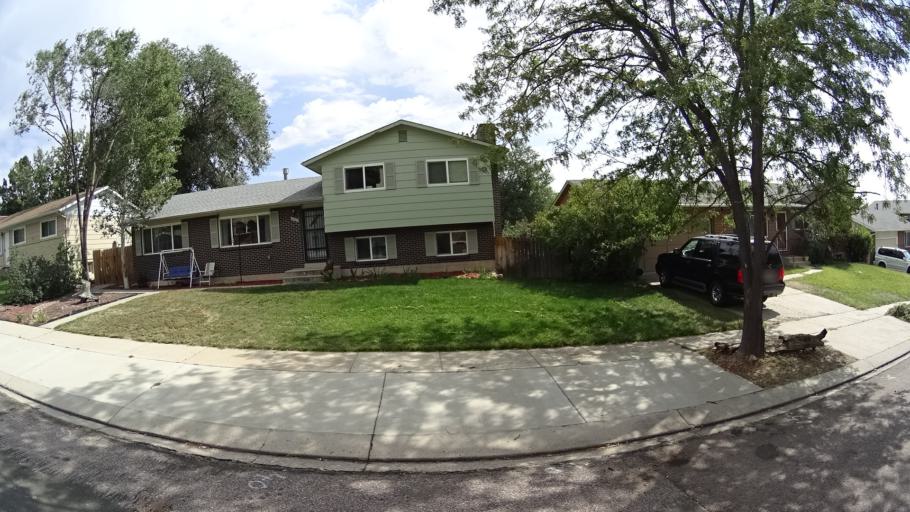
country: US
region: Colorado
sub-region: El Paso County
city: Cimarron Hills
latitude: 38.8485
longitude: -104.7302
